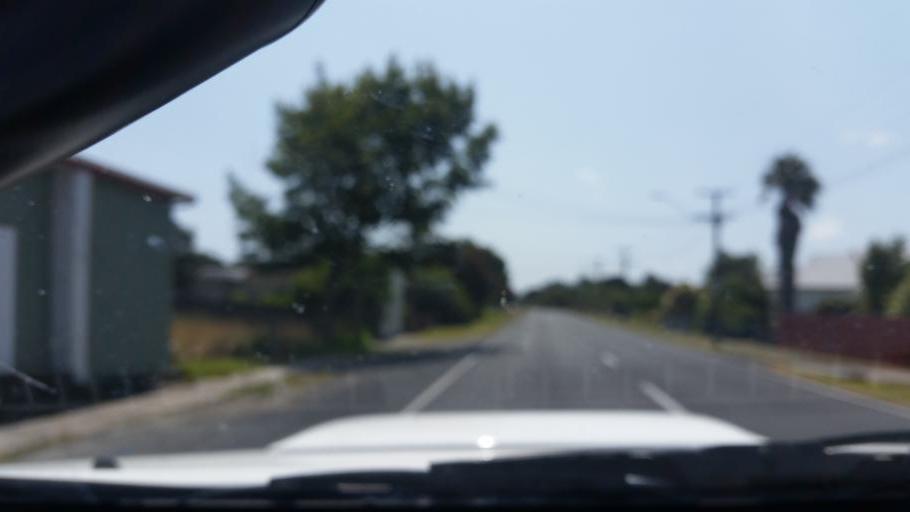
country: NZ
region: Northland
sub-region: Kaipara District
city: Dargaville
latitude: -36.0279
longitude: 173.9192
